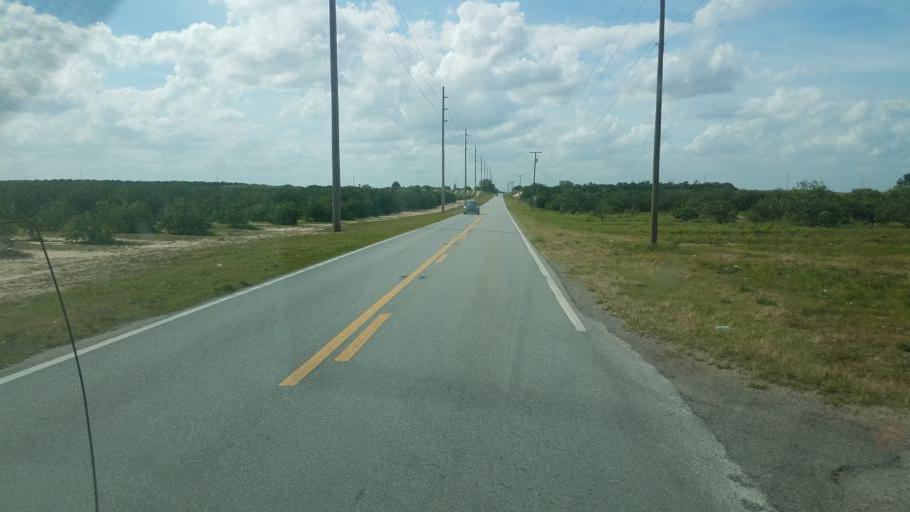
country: US
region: Florida
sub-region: Polk County
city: Lake Wales
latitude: 27.9610
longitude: -81.5699
